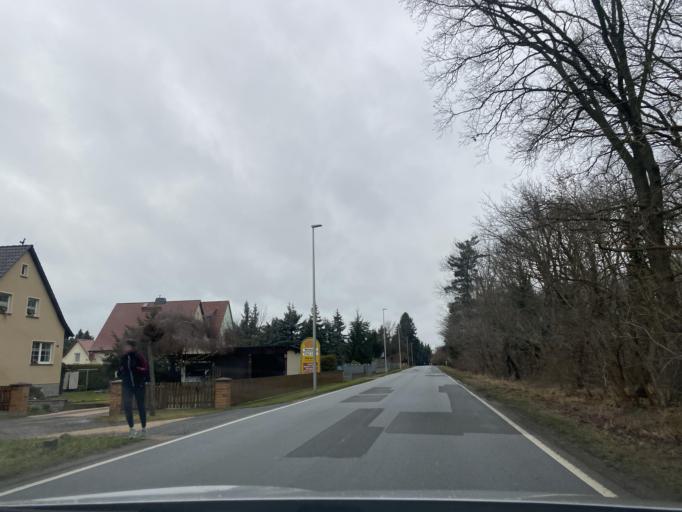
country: DE
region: Saxony
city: Rothenburg
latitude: 51.3269
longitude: 14.9735
